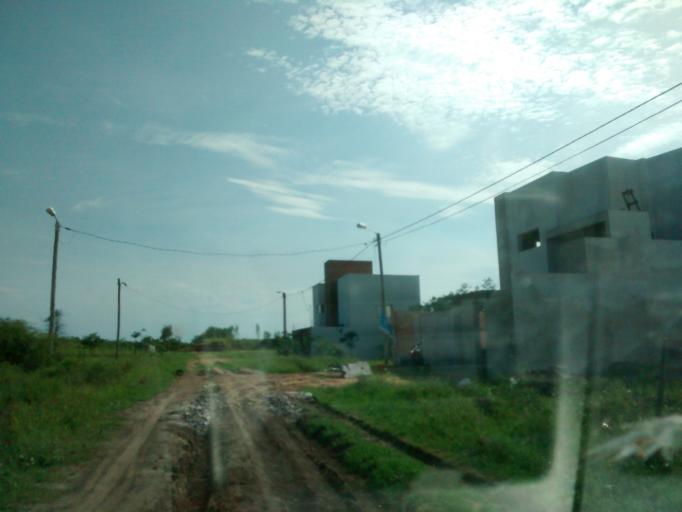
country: AR
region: Chaco
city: Resistencia
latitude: -27.4058
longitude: -58.9677
